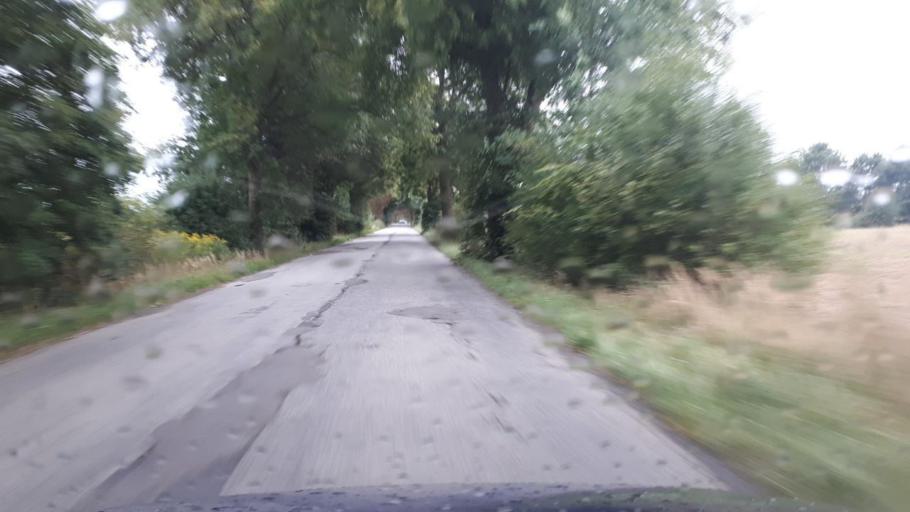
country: PL
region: Silesian Voivodeship
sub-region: Powiat tarnogorski
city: Wieszowa
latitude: 50.3751
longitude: 18.7163
